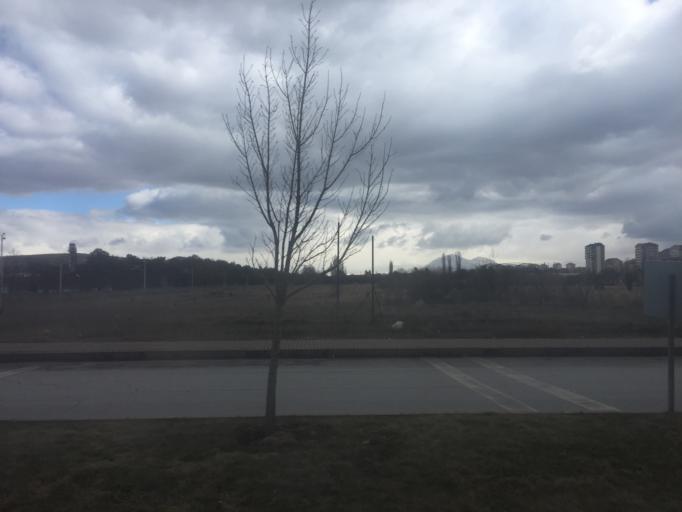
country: TR
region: Kayseri
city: Melikgazi
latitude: 38.7502
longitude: 35.4052
